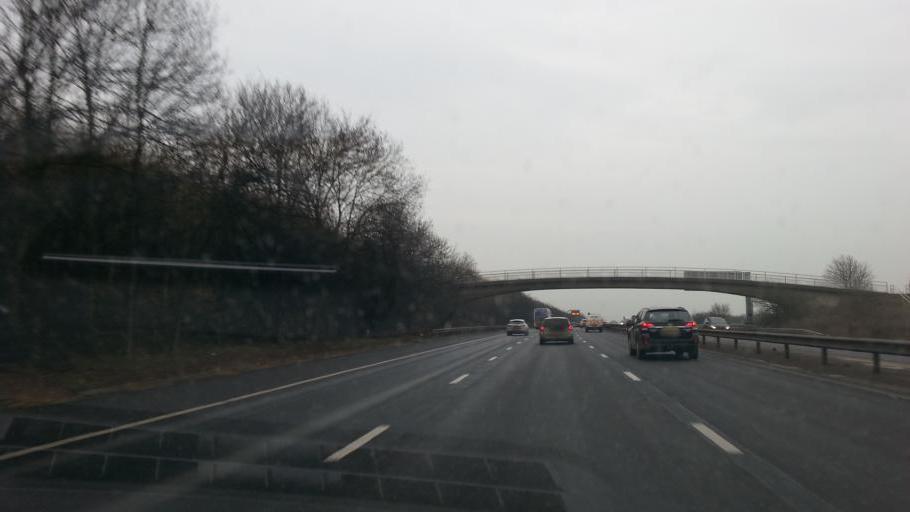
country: GB
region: England
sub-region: Essex
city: Harlow
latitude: 51.7615
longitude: 0.1495
